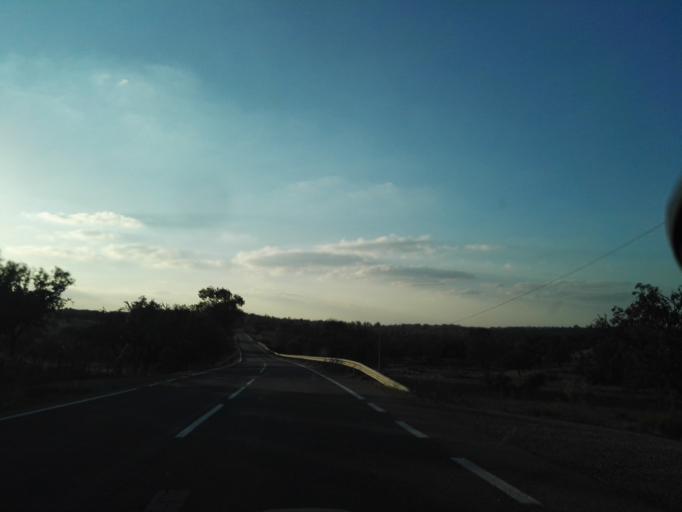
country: PT
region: Evora
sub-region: Arraiolos
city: Arraiolos
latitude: 38.8806
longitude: -7.9886
